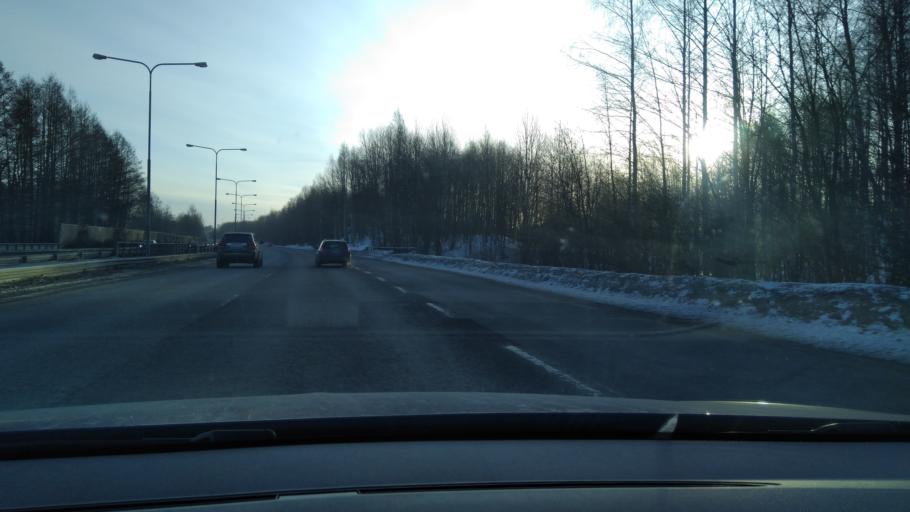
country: FI
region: Pirkanmaa
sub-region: Tampere
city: Pirkkala
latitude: 61.4989
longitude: 23.6646
